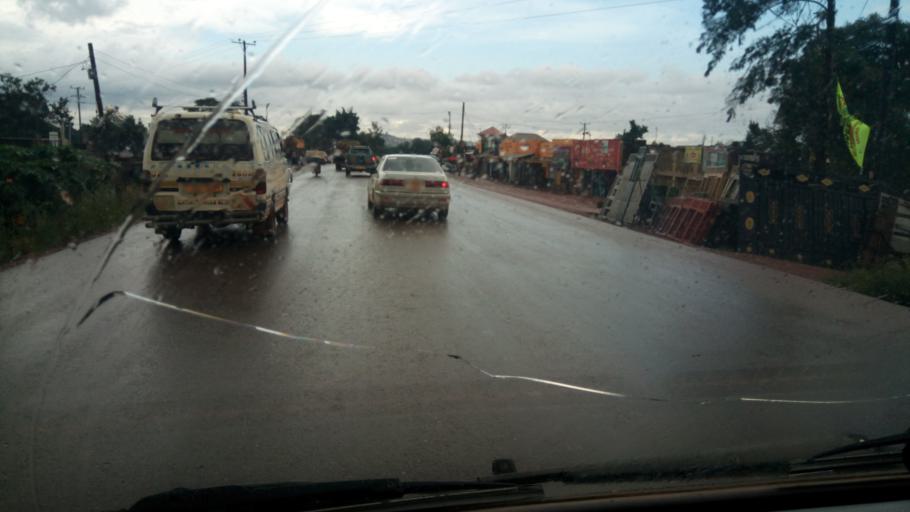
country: UG
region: Central Region
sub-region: Wakiso District
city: Wakiso
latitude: 0.3962
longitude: 32.4954
